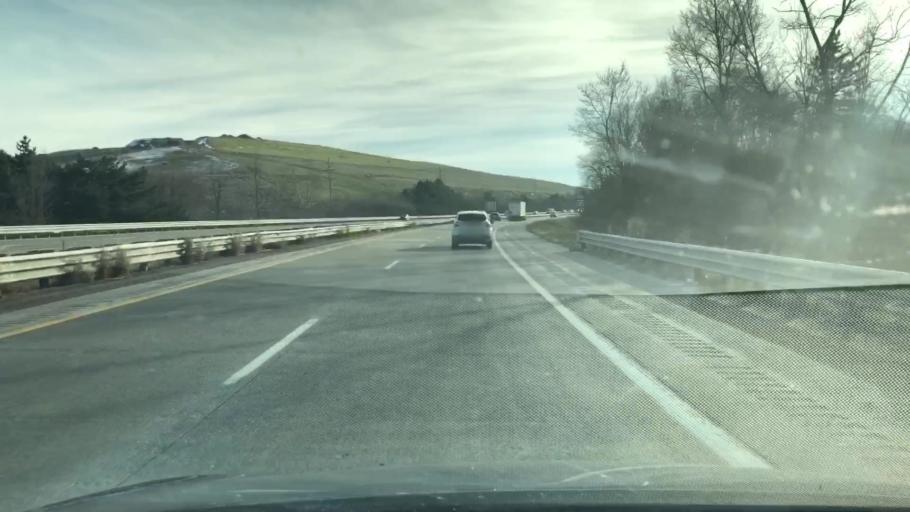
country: US
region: Michigan
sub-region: Genesee County
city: Lake Fenton
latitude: 42.9093
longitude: -83.7261
